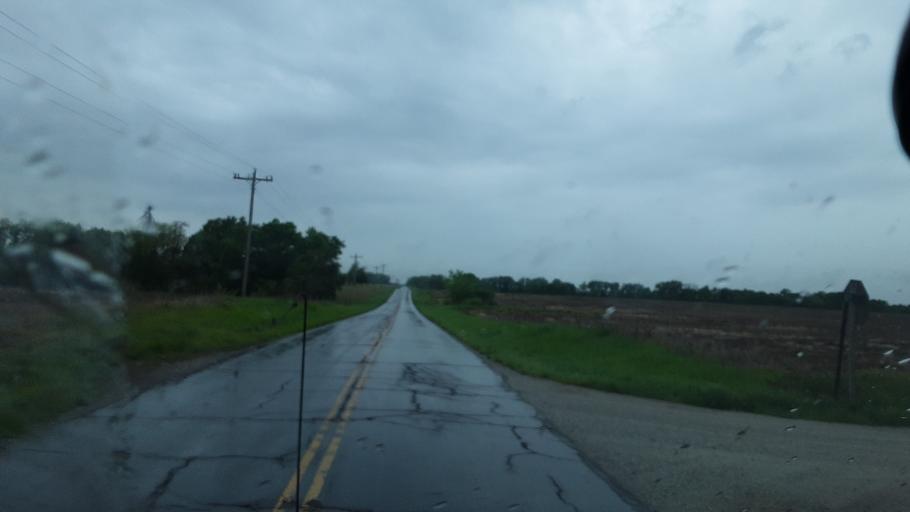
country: US
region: Missouri
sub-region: Randolph County
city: Moberly
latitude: 39.3928
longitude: -92.2385
